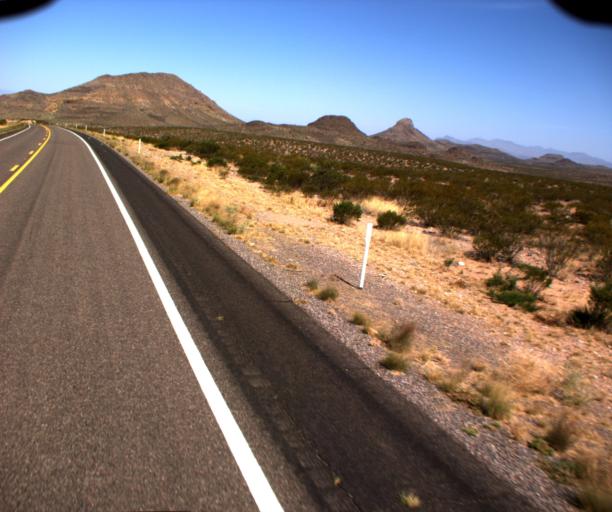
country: US
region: Arizona
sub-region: Greenlee County
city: Clifton
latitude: 32.7540
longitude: -109.3628
